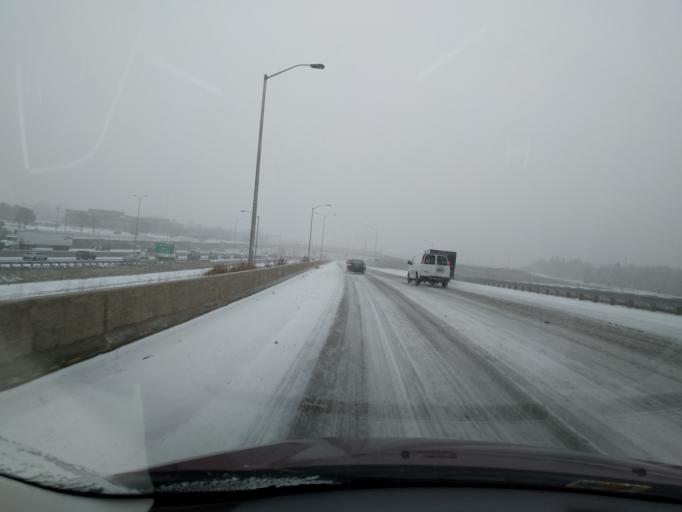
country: US
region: Wisconsin
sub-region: Waukesha County
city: Butler
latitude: 43.1579
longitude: -88.0622
